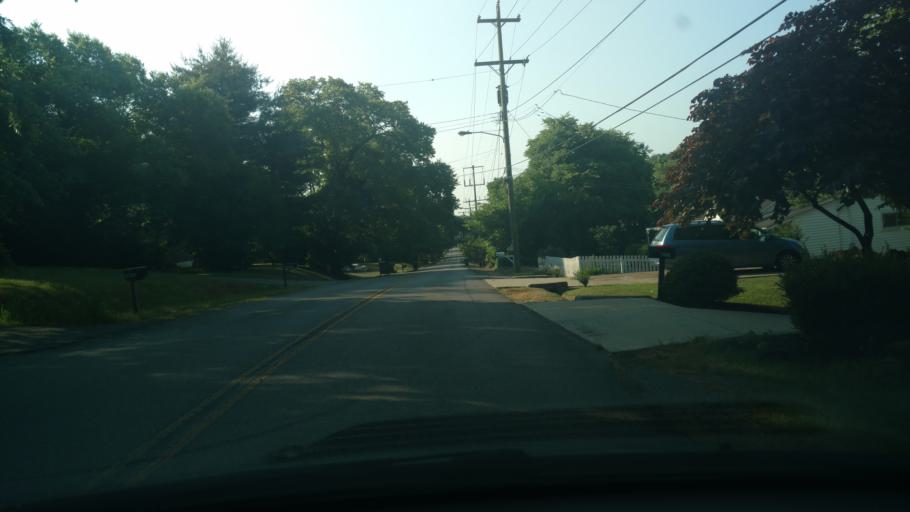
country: US
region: Tennessee
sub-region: Davidson County
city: Nashville
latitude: 36.2137
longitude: -86.7165
